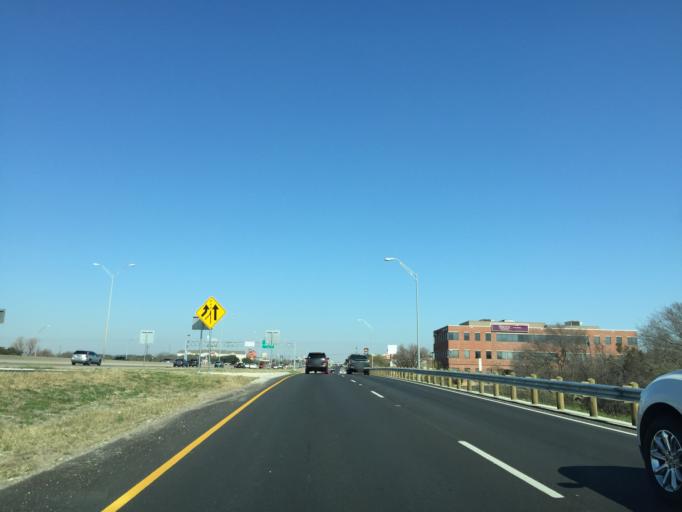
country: US
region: Texas
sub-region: Williamson County
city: Round Rock
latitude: 30.5219
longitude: -97.6887
